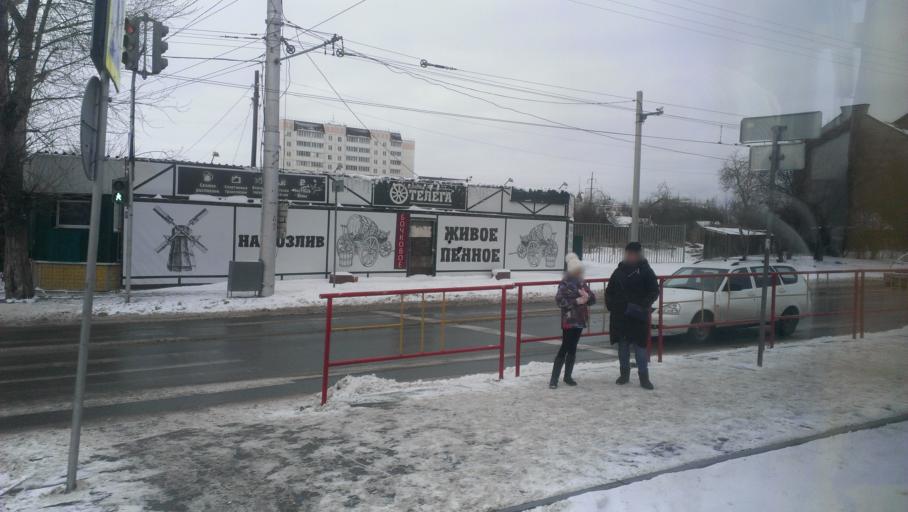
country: RU
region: Altai Krai
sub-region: Gorod Barnaulskiy
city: Barnaul
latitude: 53.3794
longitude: 83.7131
